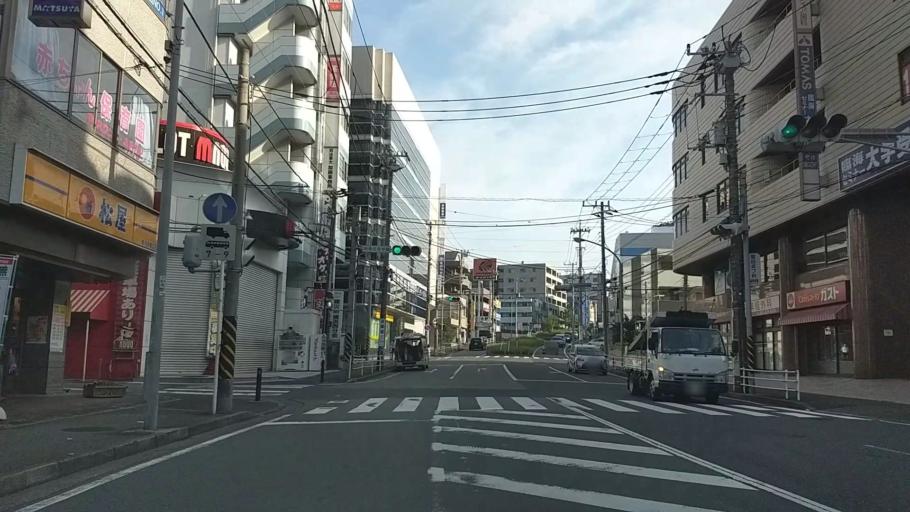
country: JP
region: Kanagawa
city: Yokohama
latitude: 35.4314
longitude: 139.5578
